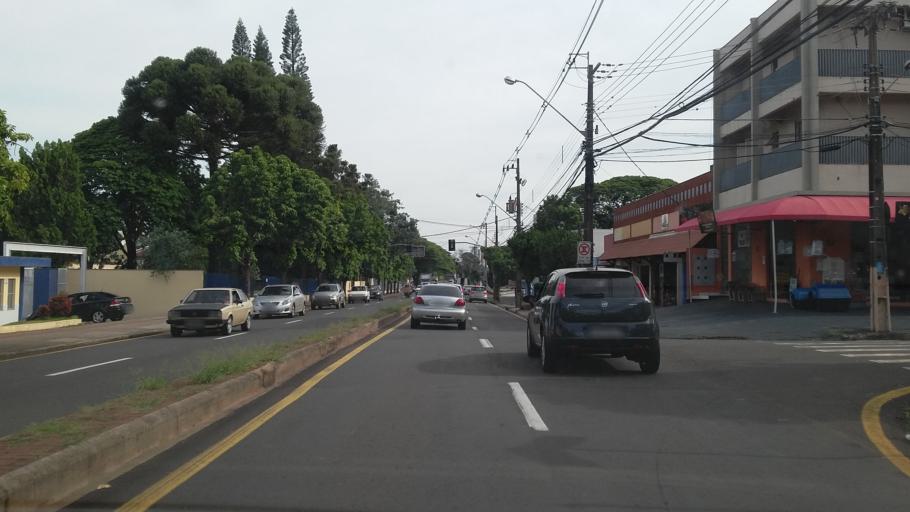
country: BR
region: Parana
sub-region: Londrina
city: Londrina
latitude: -23.3096
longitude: -51.1781
